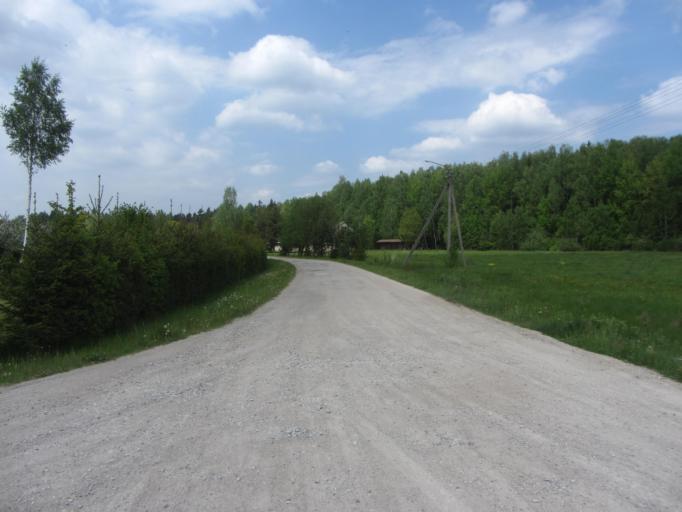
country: LT
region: Utenos apskritis
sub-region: Anyksciai
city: Anyksciai
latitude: 55.6198
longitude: 25.2823
